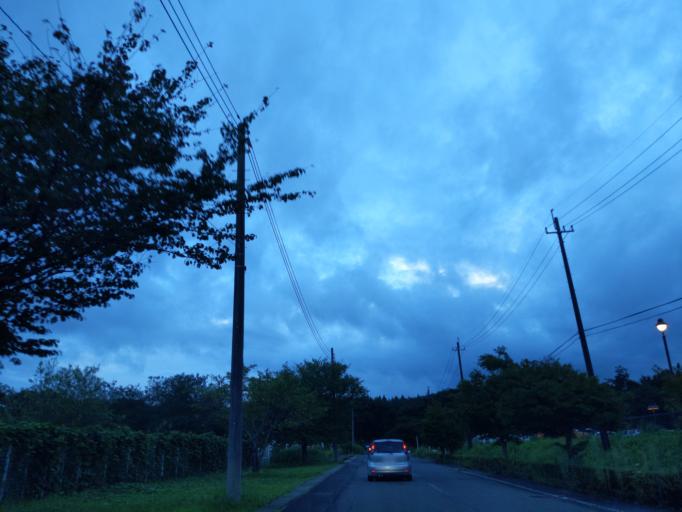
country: JP
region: Tochigi
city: Kuroiso
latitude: 36.9646
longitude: 139.9933
